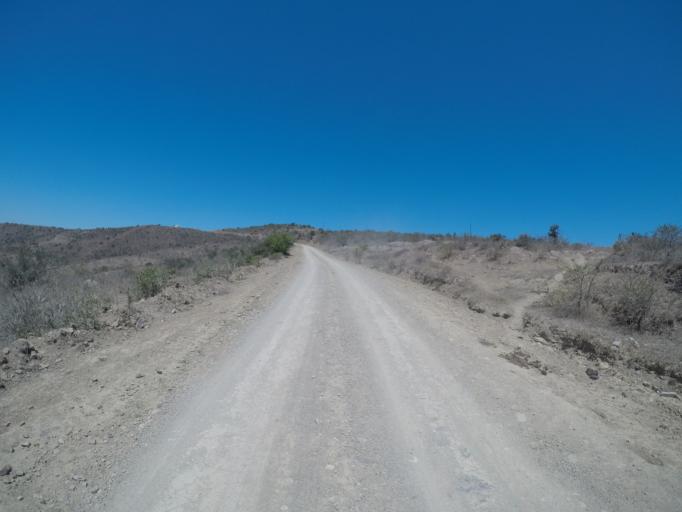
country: ZA
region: Eastern Cape
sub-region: OR Tambo District Municipality
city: Mthatha
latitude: -31.8756
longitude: 28.8727
